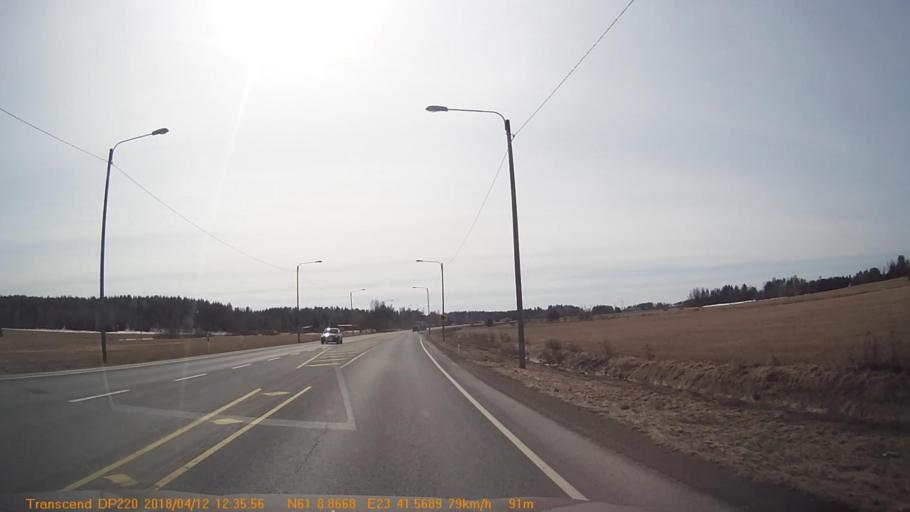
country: FI
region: Pirkanmaa
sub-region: Etelae-Pirkanmaa
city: Kylmaekoski
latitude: 61.1479
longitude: 23.6929
